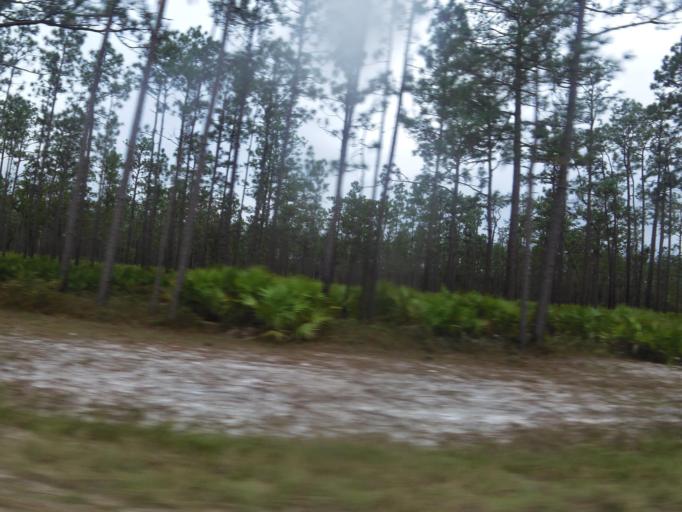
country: US
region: Georgia
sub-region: Charlton County
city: Folkston
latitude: 30.7406
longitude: -82.1340
